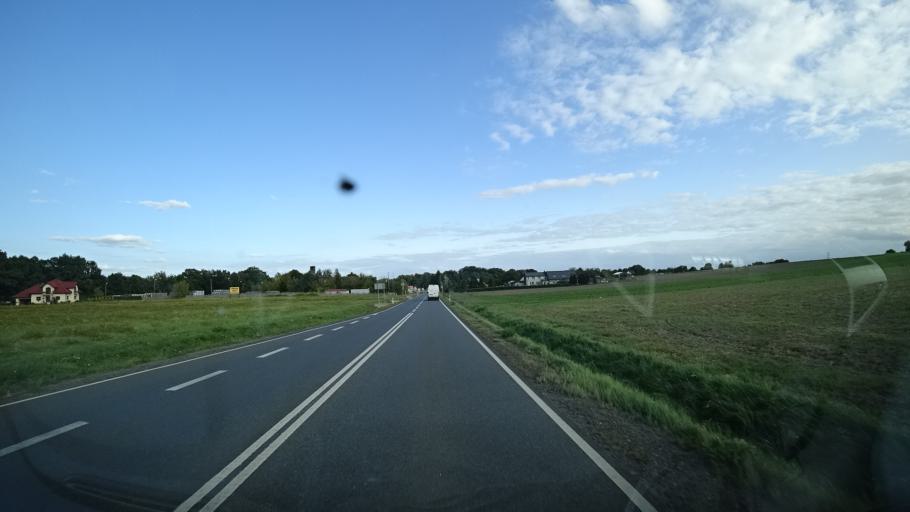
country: PL
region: Silesian Voivodeship
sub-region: Powiat gliwicki
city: Sosnicowice
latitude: 50.2769
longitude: 18.5186
